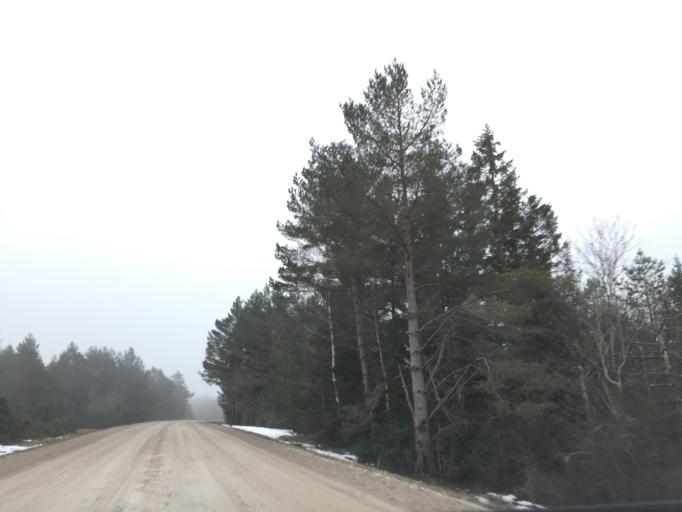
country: EE
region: Saare
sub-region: Kuressaare linn
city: Kuressaare
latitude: 58.4780
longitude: 22.0013
